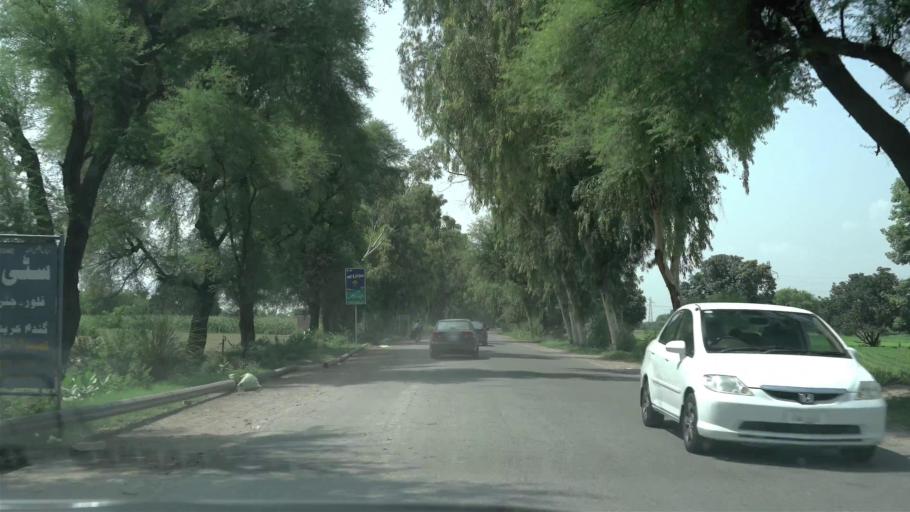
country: PK
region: Punjab
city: Gojra
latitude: 31.1700
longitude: 72.6217
